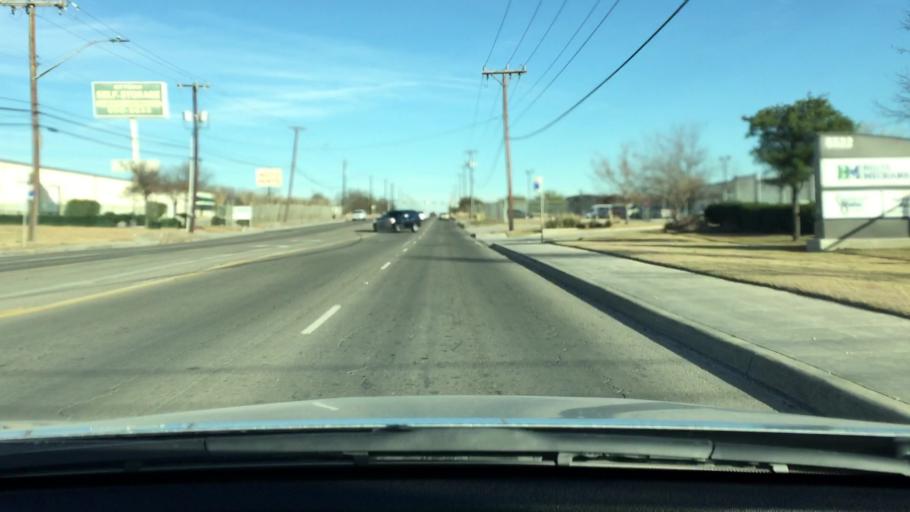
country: US
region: Texas
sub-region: Bexar County
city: Kirby
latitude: 29.4841
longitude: -98.3810
